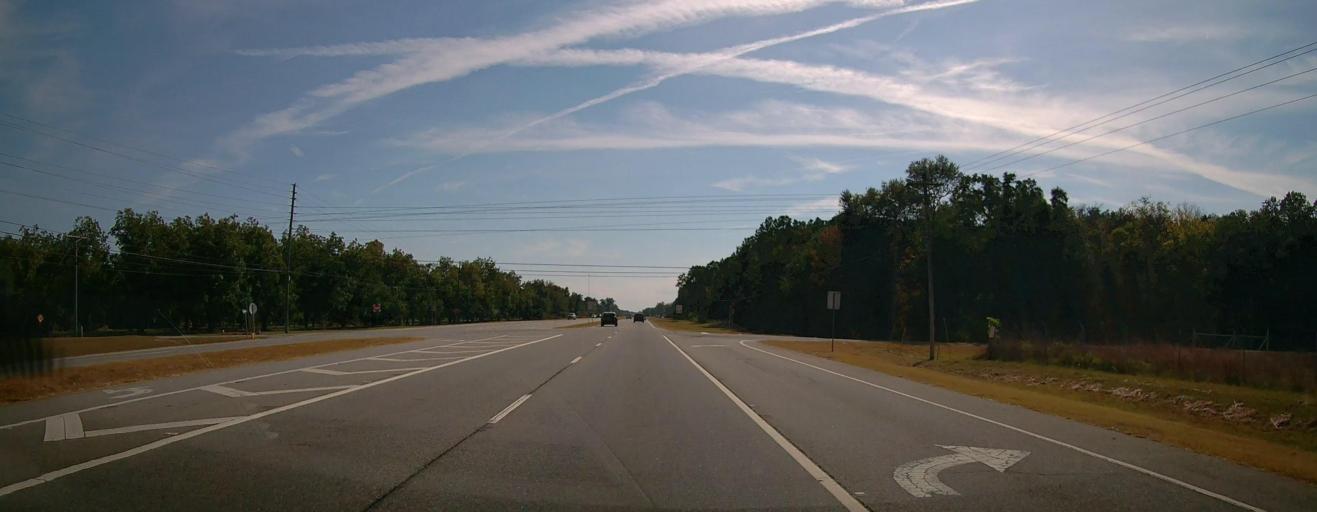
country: US
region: Georgia
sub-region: Dougherty County
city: Putney
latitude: 31.5173
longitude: -84.1157
